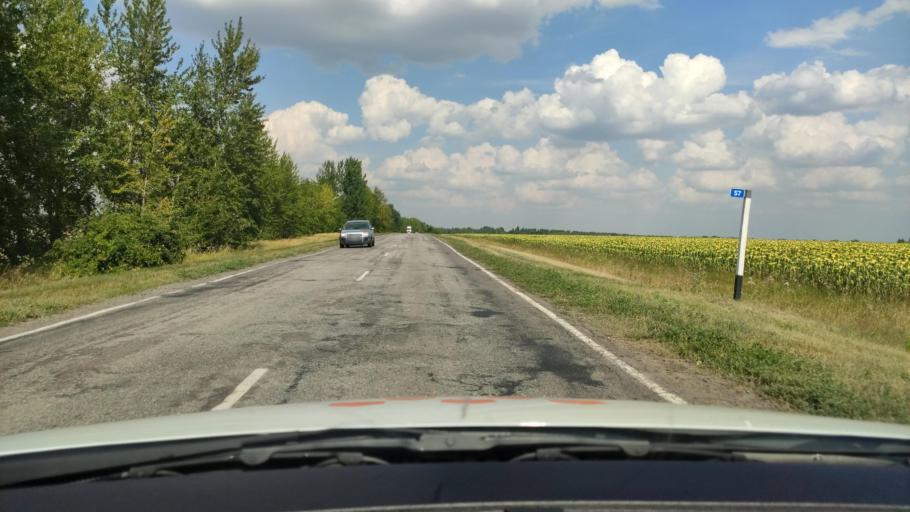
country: RU
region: Voronezj
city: Pereleshinskiy
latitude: 51.7499
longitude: 40.4140
